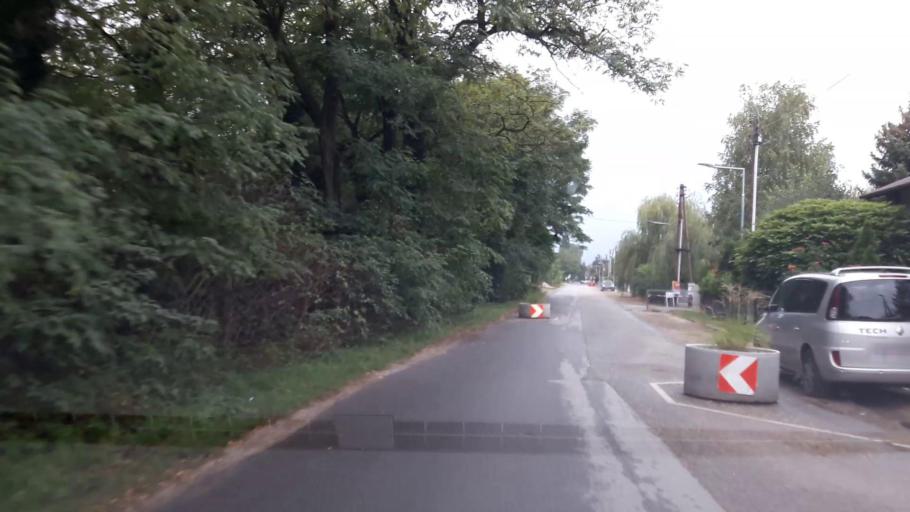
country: AT
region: Lower Austria
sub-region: Politischer Bezirk Ganserndorf
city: Strasshof an der Nordbahn
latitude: 48.3207
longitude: 16.6377
